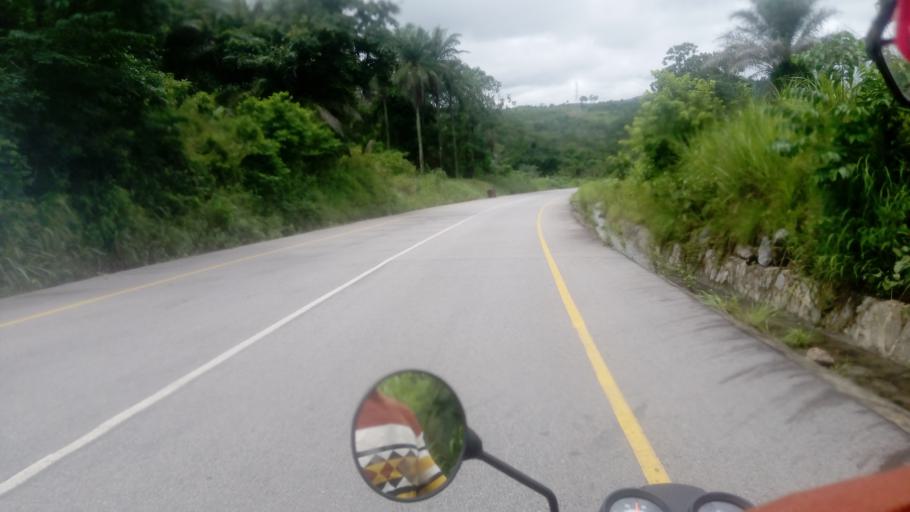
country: SL
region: Northern Province
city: Masaka
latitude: 8.6595
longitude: -11.7836
